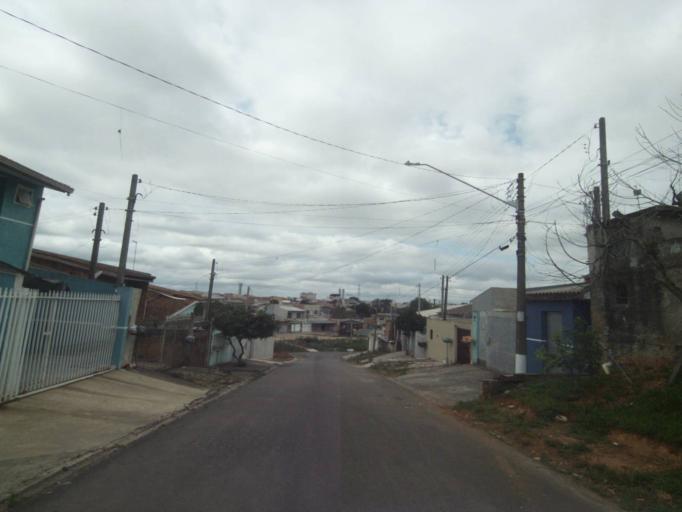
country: BR
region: Parana
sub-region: Sao Jose Dos Pinhais
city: Sao Jose dos Pinhais
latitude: -25.5487
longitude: -49.2518
